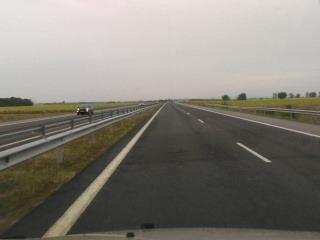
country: BG
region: Stara Zagora
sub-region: Obshtina Radnevo
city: Radnevo
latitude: 42.3771
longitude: 25.8248
